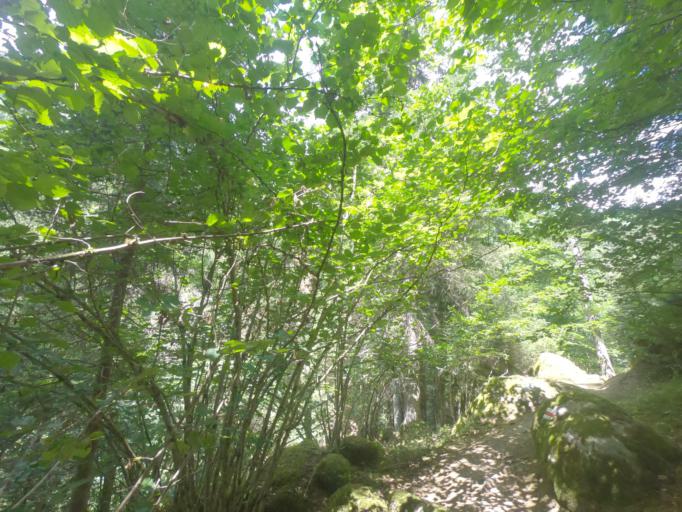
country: CH
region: Valais
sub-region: Saint-Maurice District
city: Salvan
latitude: 46.0753
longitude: 6.9732
